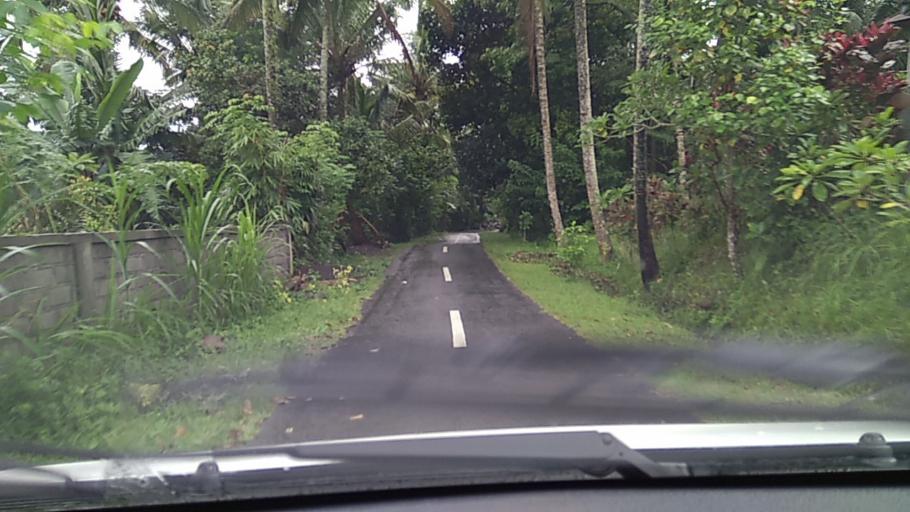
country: ID
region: Bali
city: Tiyingtali Kelod
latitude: -8.4045
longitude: 115.6281
